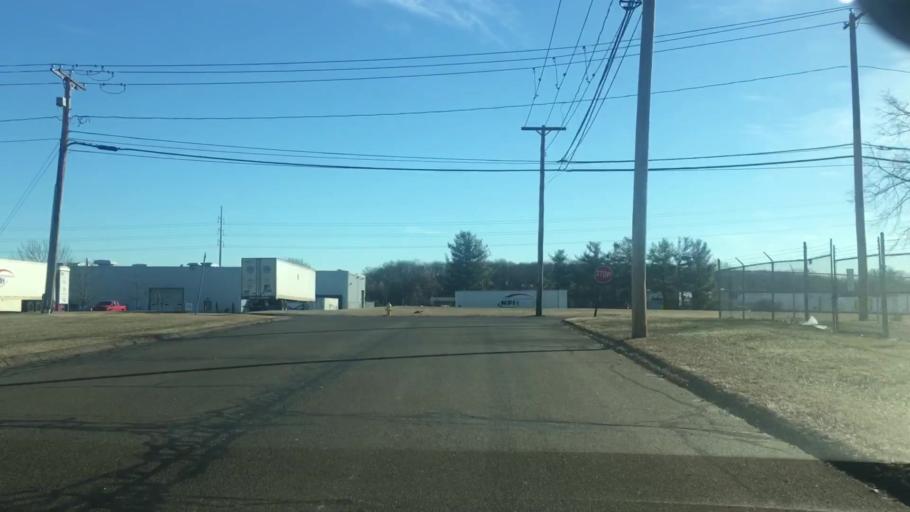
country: US
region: Connecticut
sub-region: New Haven County
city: North Haven
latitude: 41.4210
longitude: -72.8443
